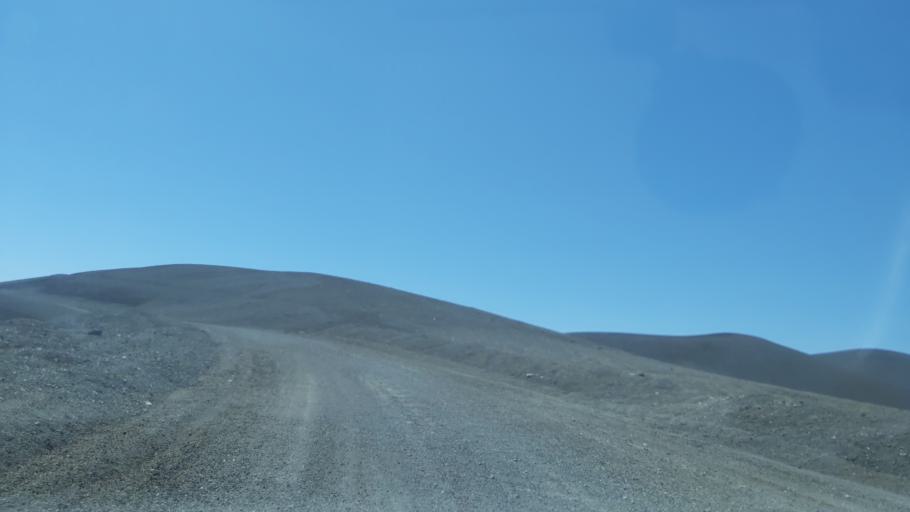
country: CL
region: Araucania
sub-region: Provincia de Cautin
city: Vilcun
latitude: -38.3734
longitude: -71.5390
